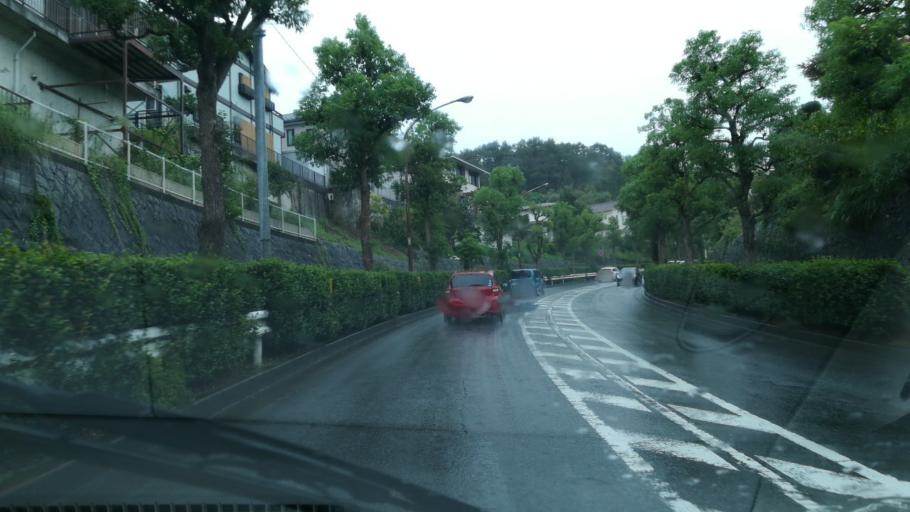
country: JP
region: Tokyo
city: Hino
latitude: 35.6436
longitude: 139.3875
